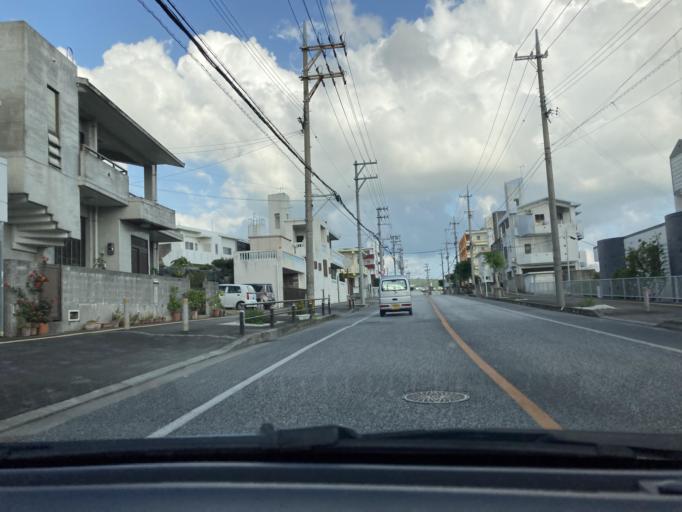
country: JP
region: Okinawa
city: Itoman
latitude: 26.1303
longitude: 127.6761
